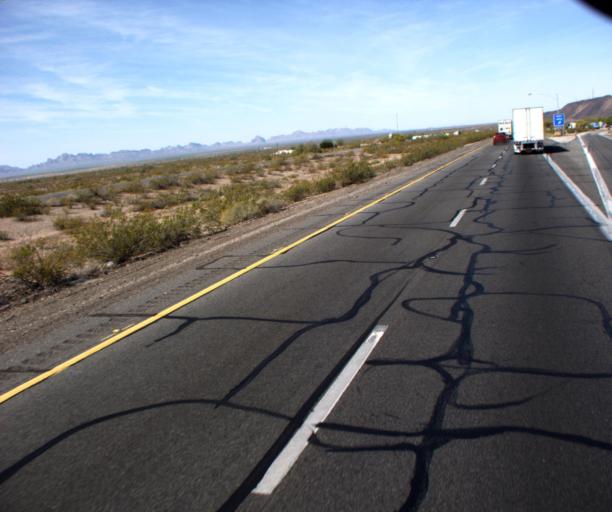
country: US
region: Arizona
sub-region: Maricopa County
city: Buckeye
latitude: 33.5197
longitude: -113.0627
